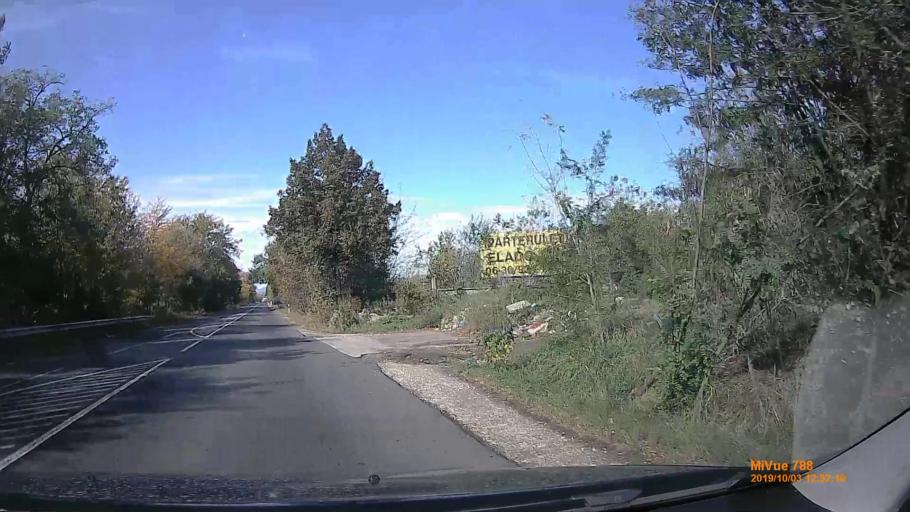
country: HU
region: Pest
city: Szod
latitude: 47.7479
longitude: 19.1730
